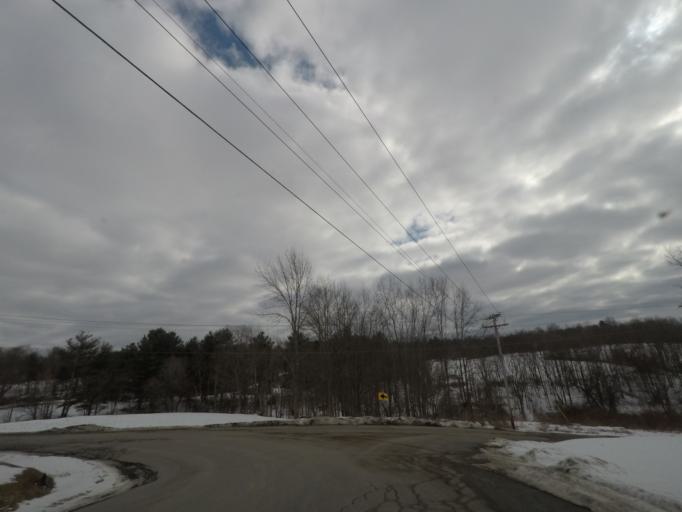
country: US
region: New York
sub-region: Rensselaer County
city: Hoosick Falls
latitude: 42.9188
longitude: -73.4322
